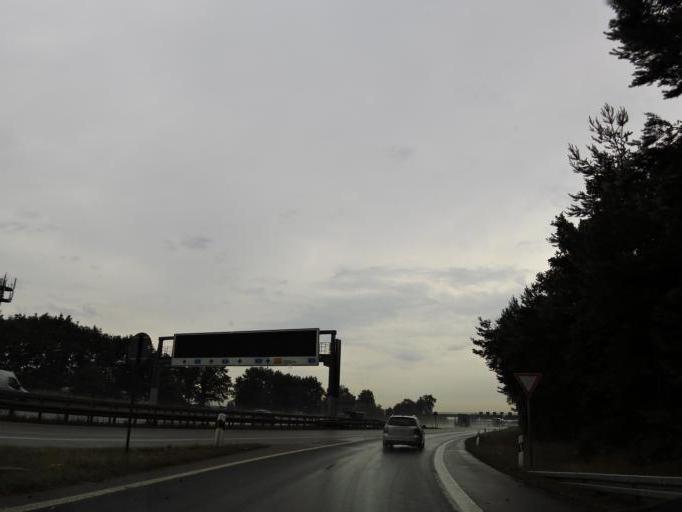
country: DE
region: Hesse
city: Morfelden-Walldorf
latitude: 50.0365
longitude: 8.5966
